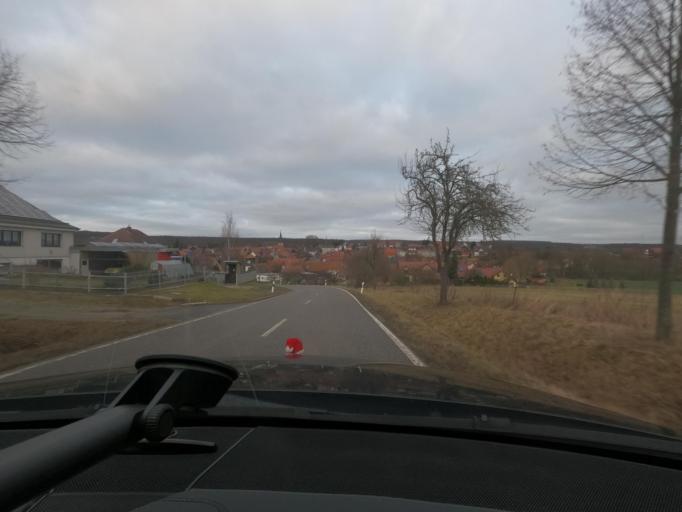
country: DE
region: Thuringia
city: Helmsdorf
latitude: 51.2756
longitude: 10.4045
